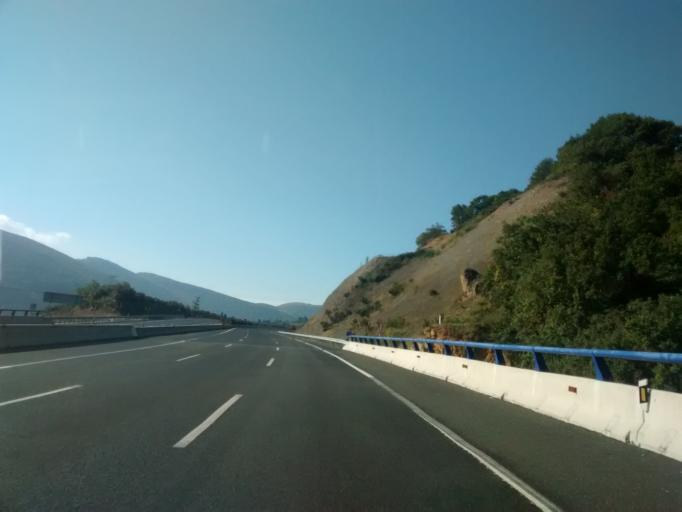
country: ES
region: Cantabria
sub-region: Provincia de Cantabria
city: Barcena de Pie de Concha
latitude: 43.1360
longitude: -4.0672
